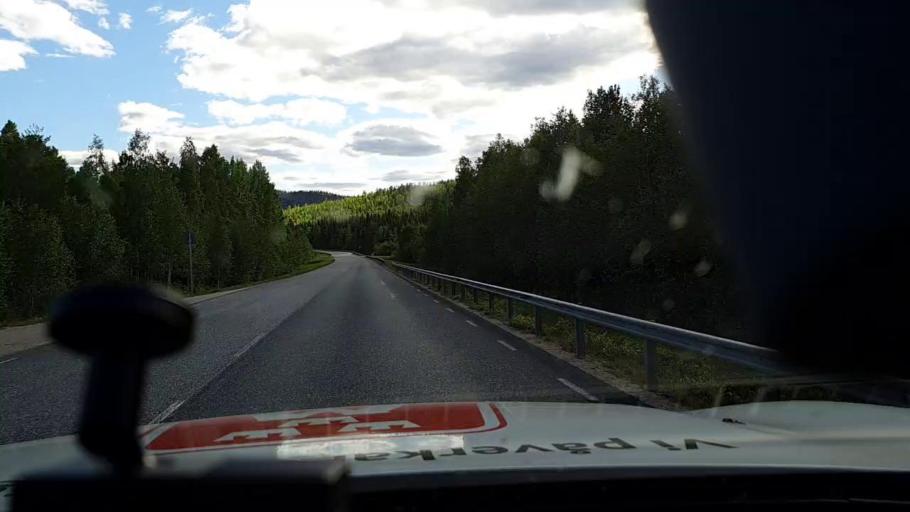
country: FI
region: Lapland
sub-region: Torniolaakso
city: Ylitornio
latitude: 66.3292
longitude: 23.6313
